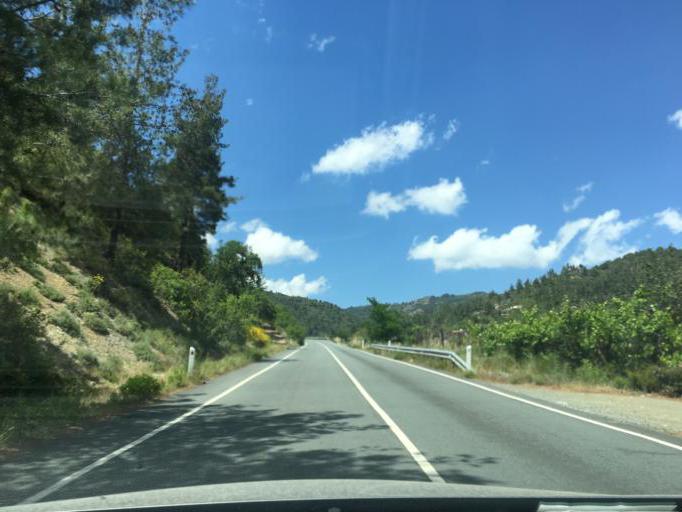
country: CY
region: Limassol
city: Pelendri
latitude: 34.9078
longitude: 32.9431
